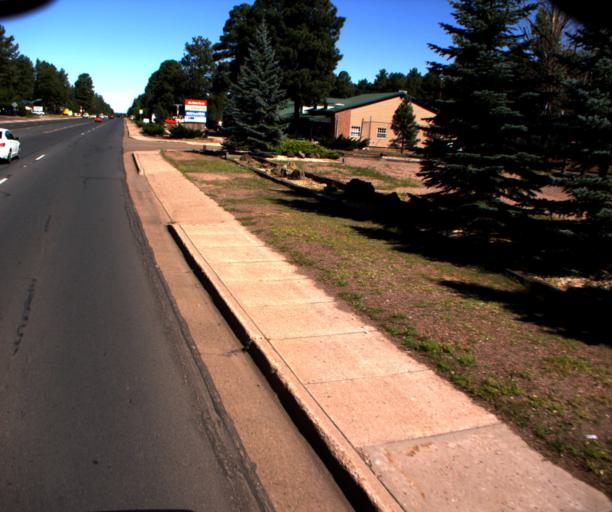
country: US
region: Arizona
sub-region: Navajo County
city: Pinetop-Lakeside
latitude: 34.1284
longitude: -109.9452
